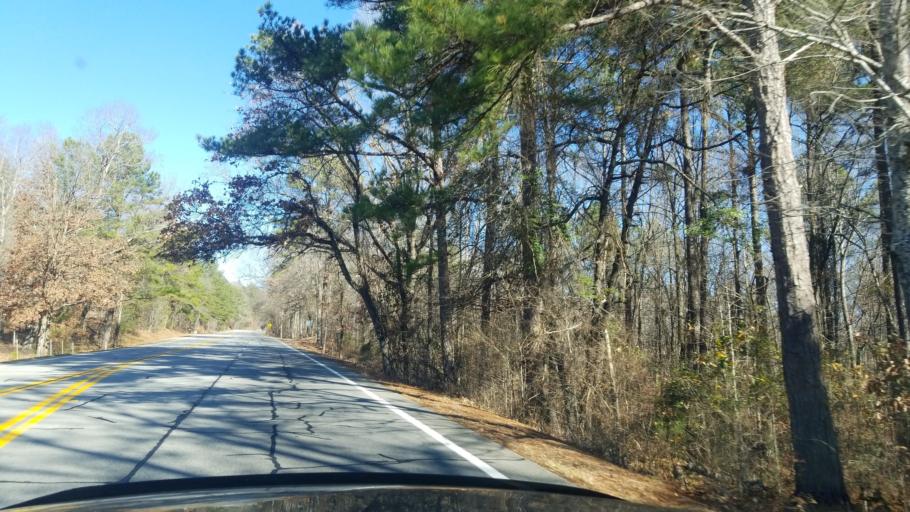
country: US
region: Georgia
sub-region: Harris County
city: Hamilton
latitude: 32.8021
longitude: -84.8636
